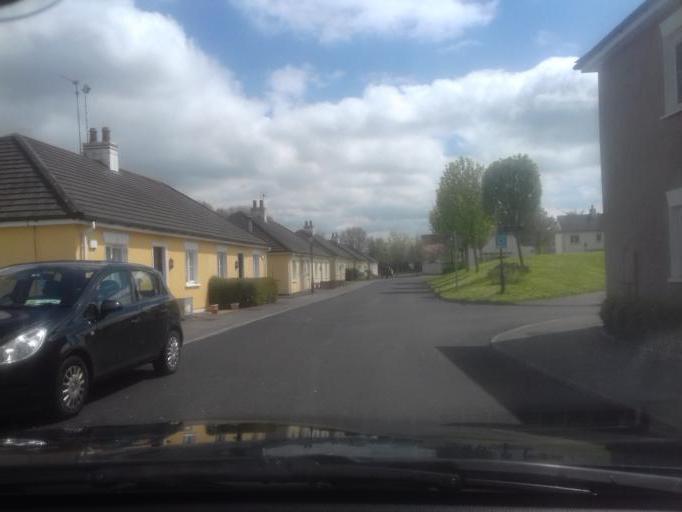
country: IE
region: Leinster
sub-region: Laois
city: Portlaoise
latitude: 53.0484
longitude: -7.3185
